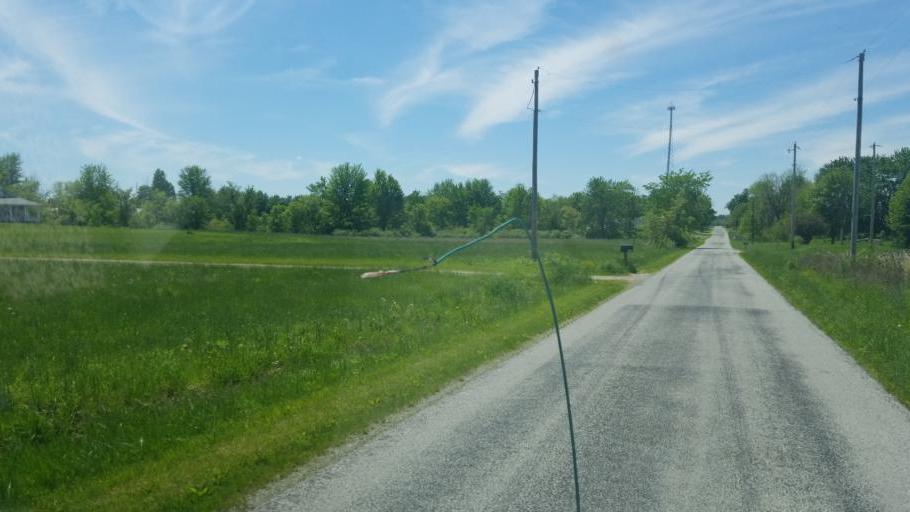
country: US
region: Ohio
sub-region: Huron County
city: Norwalk
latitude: 41.1194
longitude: -82.6081
